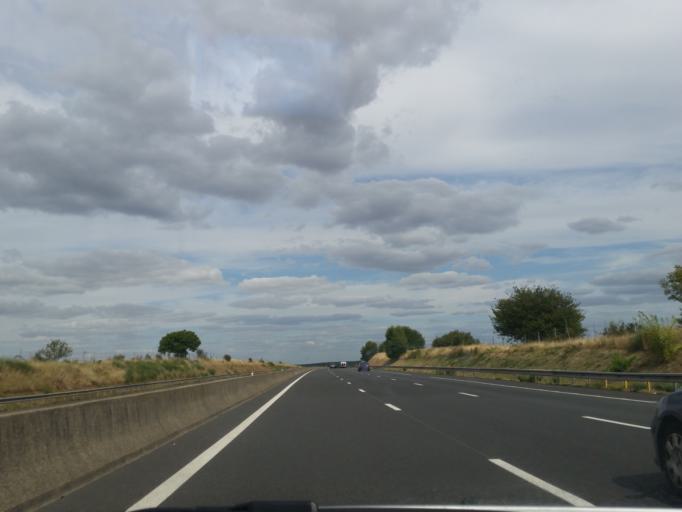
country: FR
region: Centre
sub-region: Departement d'Indre-et-Loire
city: Reugny
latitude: 47.5044
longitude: 0.8683
